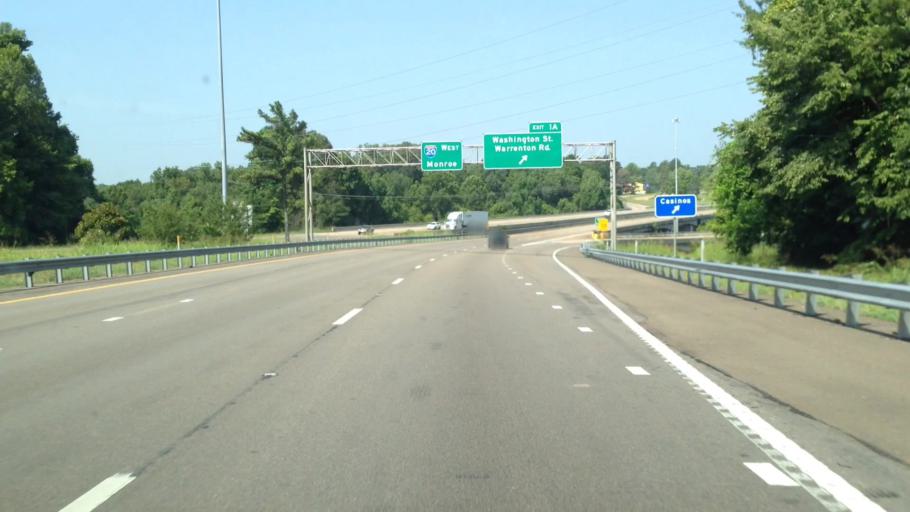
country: US
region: Mississippi
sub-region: Warren County
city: Vicksburg
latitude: 32.3109
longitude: -90.8935
